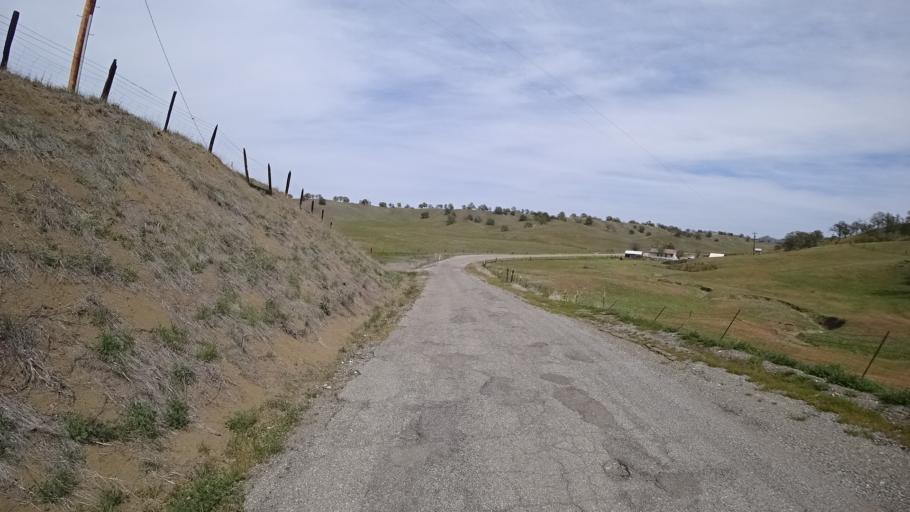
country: US
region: California
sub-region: Glenn County
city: Willows
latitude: 39.6132
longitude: -122.5733
